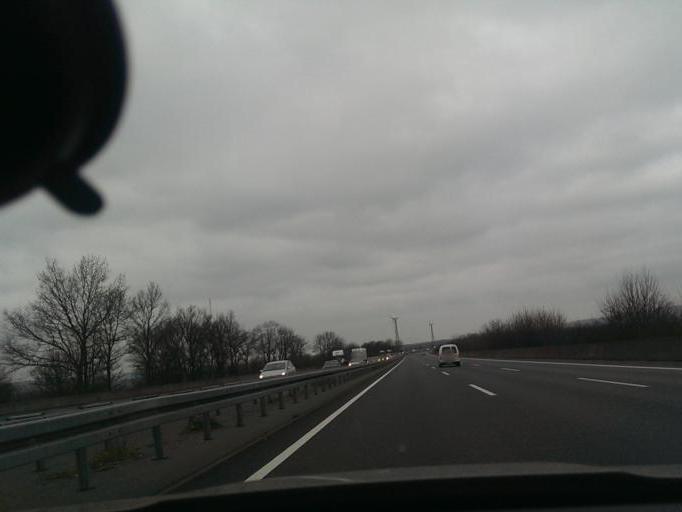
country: DE
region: Lower Saxony
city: Rehren
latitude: 52.2440
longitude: 9.2857
